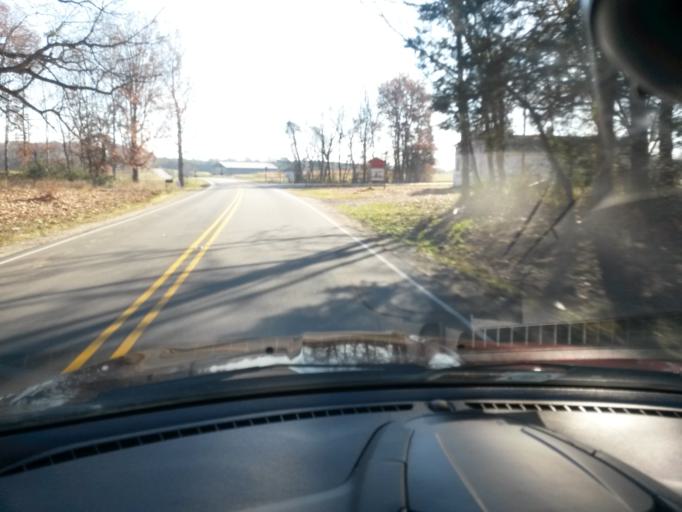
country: US
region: Virginia
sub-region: Charlotte County
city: Charlotte Court House
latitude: 37.1343
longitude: -78.6897
